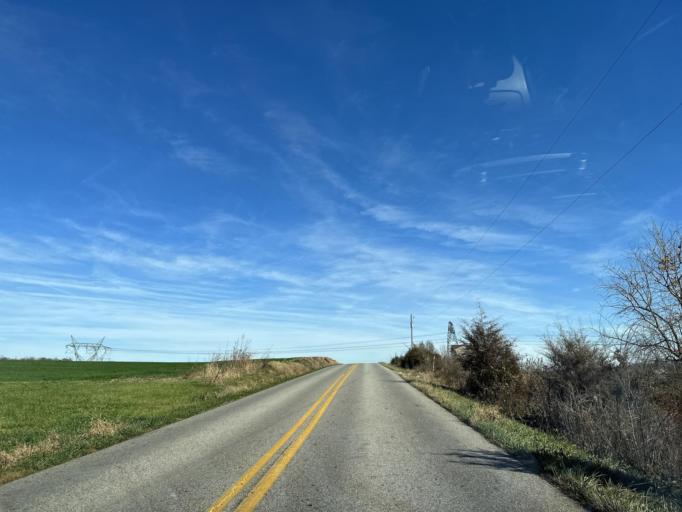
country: US
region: Virginia
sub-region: Augusta County
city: Fishersville
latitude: 38.1549
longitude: -78.9276
